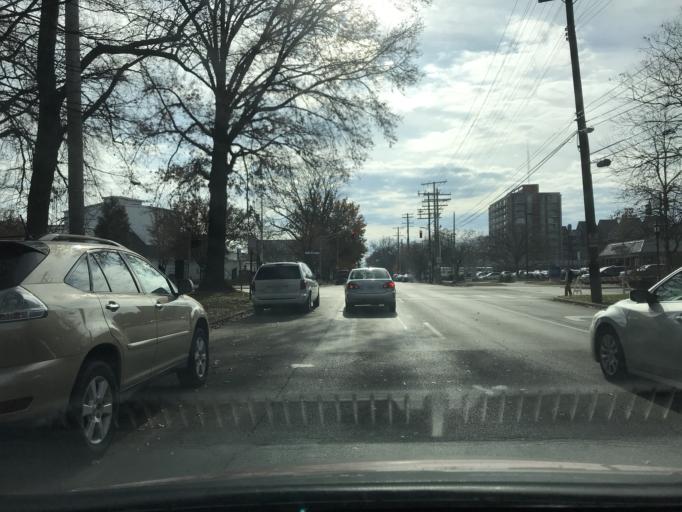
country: US
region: Kentucky
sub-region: Jefferson County
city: Louisville
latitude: 38.2210
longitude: -85.7611
